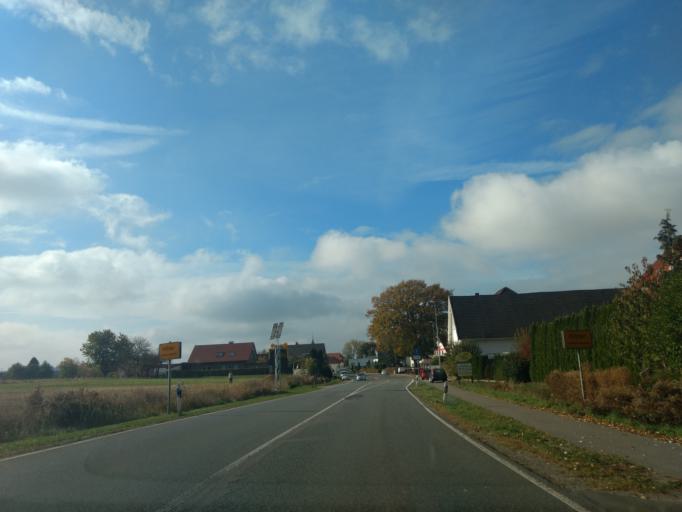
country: DE
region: Lower Saxony
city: Hilter
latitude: 52.1423
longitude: 8.1498
